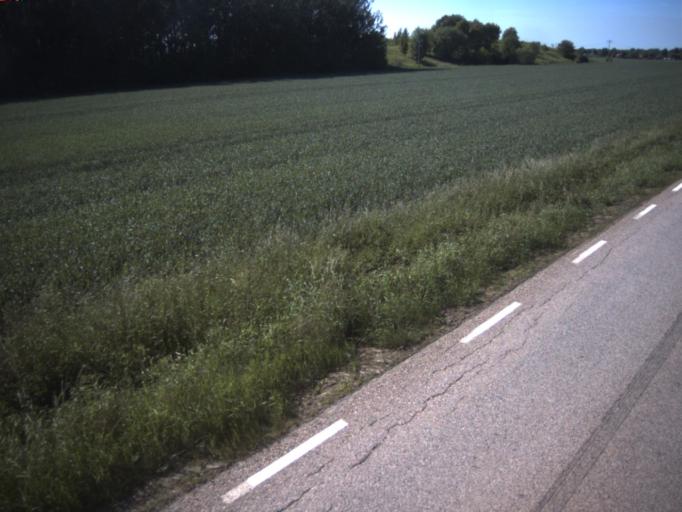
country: SE
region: Skane
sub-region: Helsingborg
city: Gantofta
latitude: 55.9794
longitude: 12.8125
